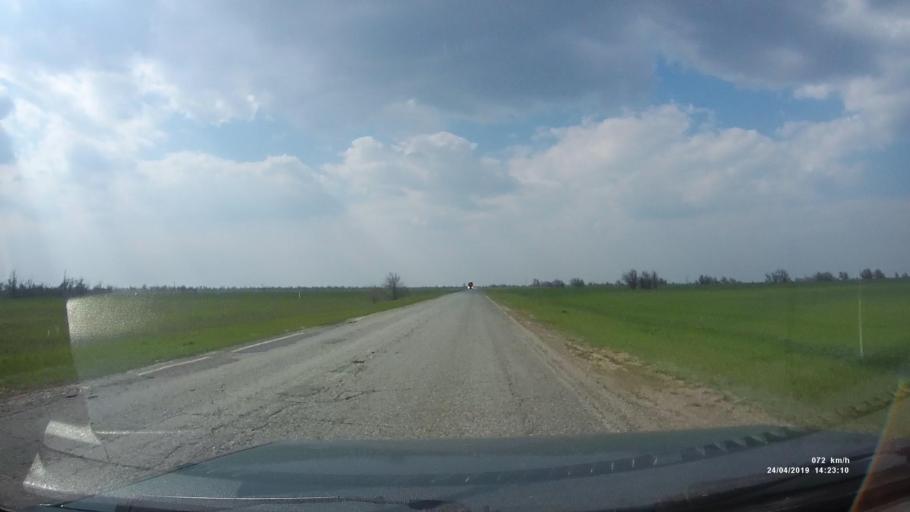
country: RU
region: Kalmykiya
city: Arshan'
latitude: 46.3197
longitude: 44.1179
